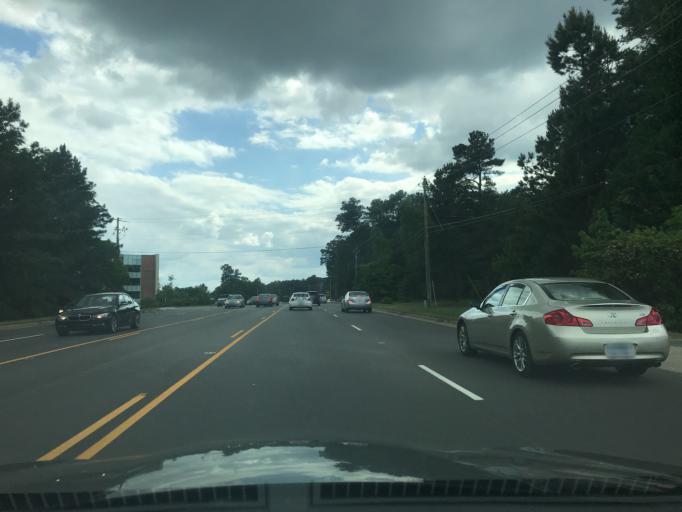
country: US
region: North Carolina
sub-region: Wake County
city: Wake Forest
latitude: 35.9110
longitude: -78.5978
